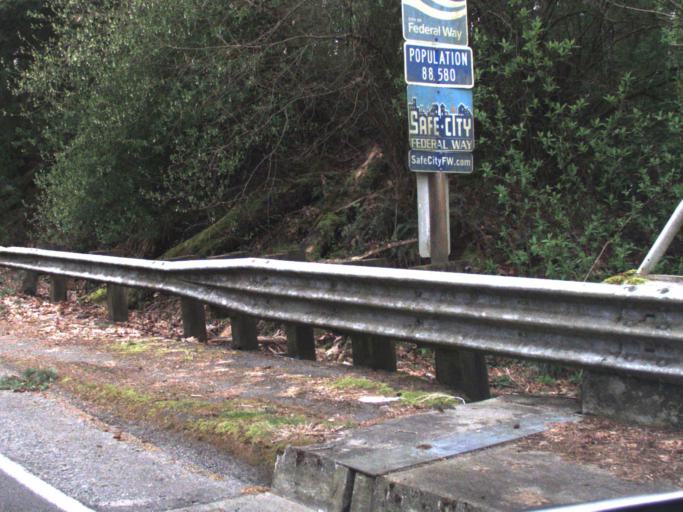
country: US
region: Washington
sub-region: Pierce County
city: Tacoma
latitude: 47.3177
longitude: -122.4123
